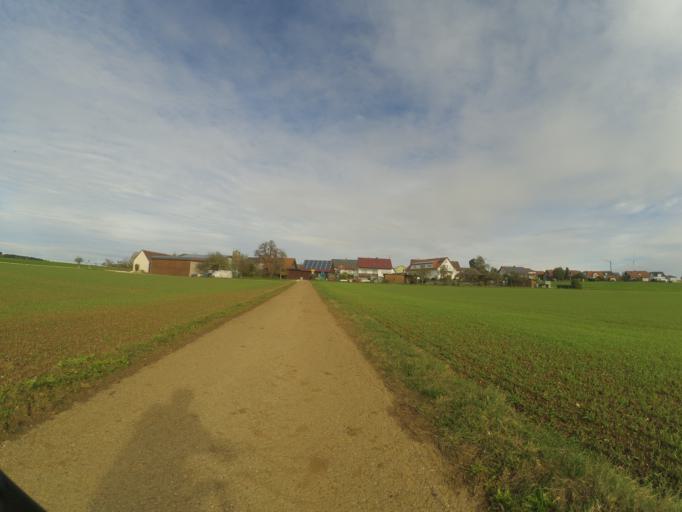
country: DE
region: Baden-Wuerttemberg
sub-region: Tuebingen Region
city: Lonsee
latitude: 48.5593
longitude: 9.9261
